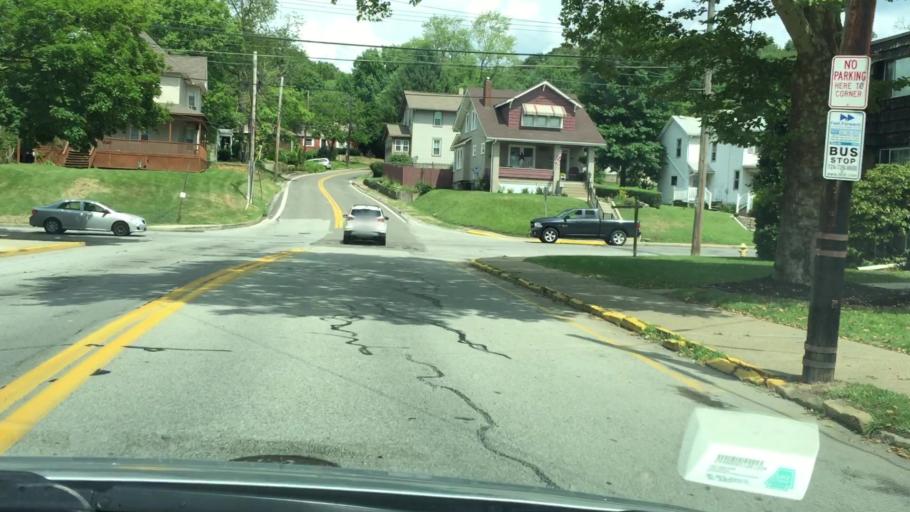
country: US
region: Pennsylvania
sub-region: Beaver County
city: Beaver
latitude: 40.6975
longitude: -80.3096
